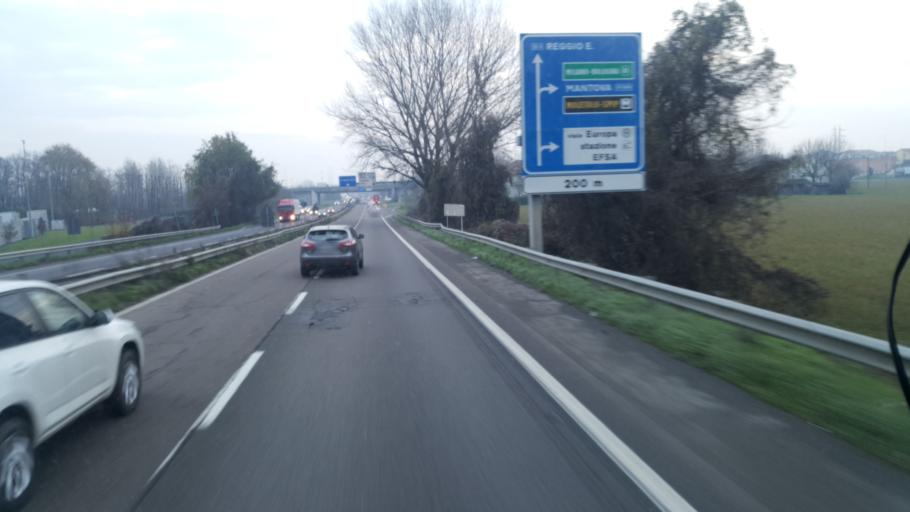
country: IT
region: Emilia-Romagna
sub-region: Provincia di Parma
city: Parma
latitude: 44.8219
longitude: 10.3232
